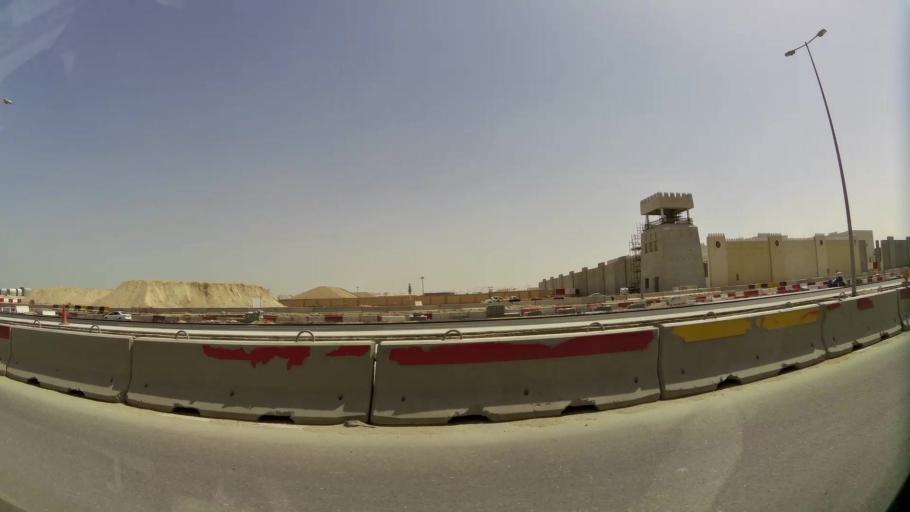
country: QA
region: Baladiyat Umm Salal
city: Umm Salal Muhammad
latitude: 25.3714
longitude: 51.4593
